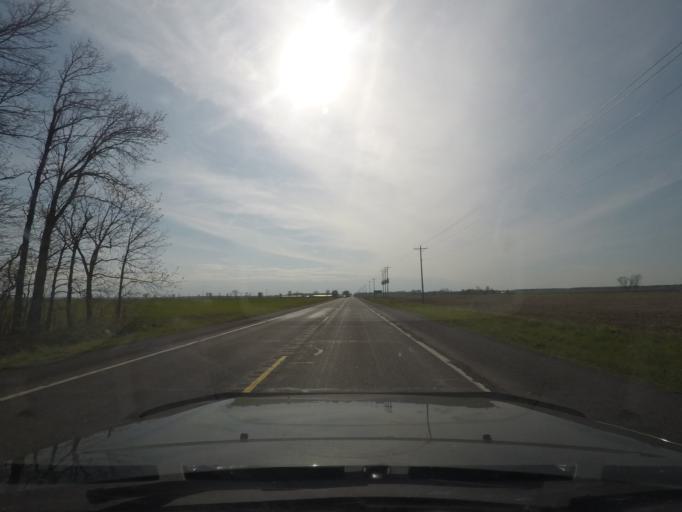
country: US
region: Michigan
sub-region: Berrien County
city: Three Oaks
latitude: 41.7982
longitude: -86.5390
